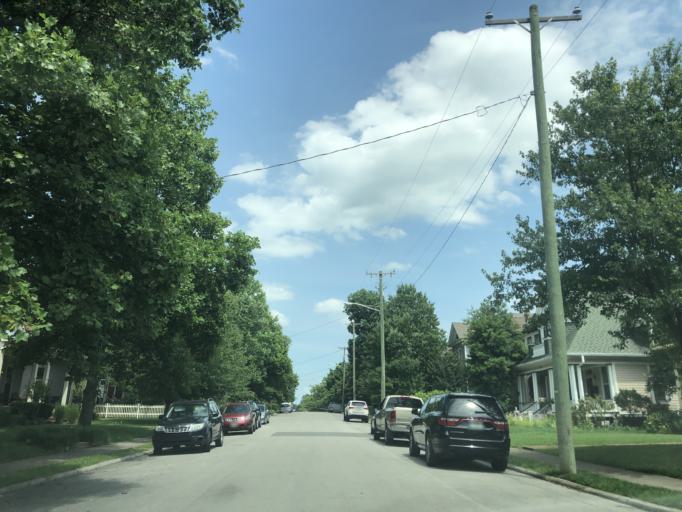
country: US
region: Tennessee
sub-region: Davidson County
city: Nashville
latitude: 36.1794
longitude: -86.7478
